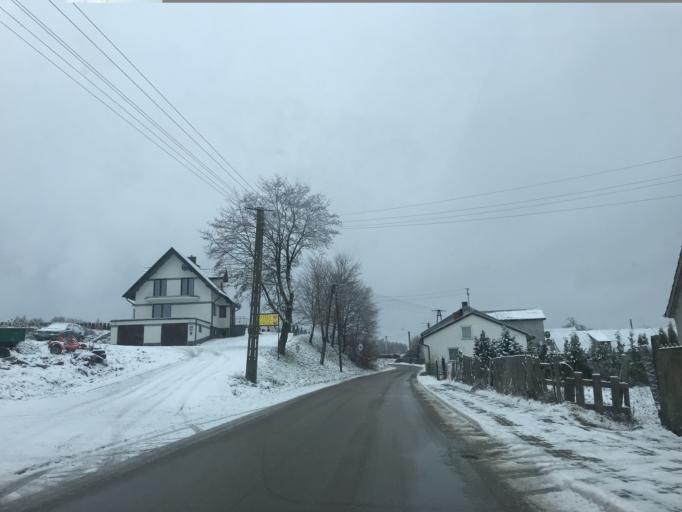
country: PL
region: Pomeranian Voivodeship
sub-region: Powiat bytowski
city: Bytow
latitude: 54.2178
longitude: 17.5620
